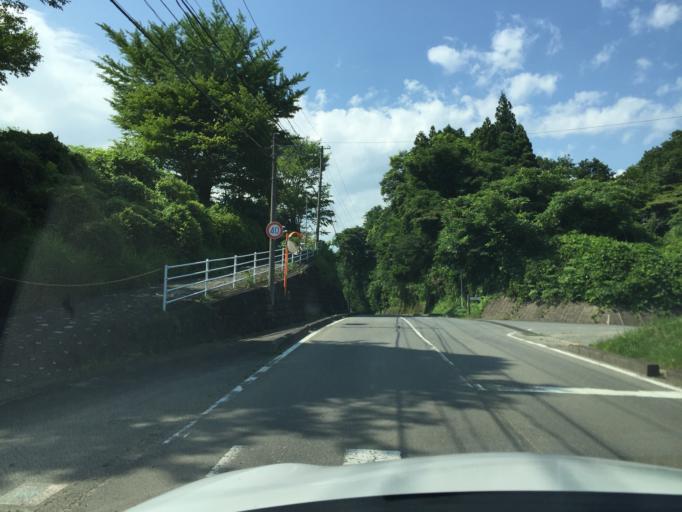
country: JP
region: Ibaraki
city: Kitaibaraki
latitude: 36.9636
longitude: 140.7034
